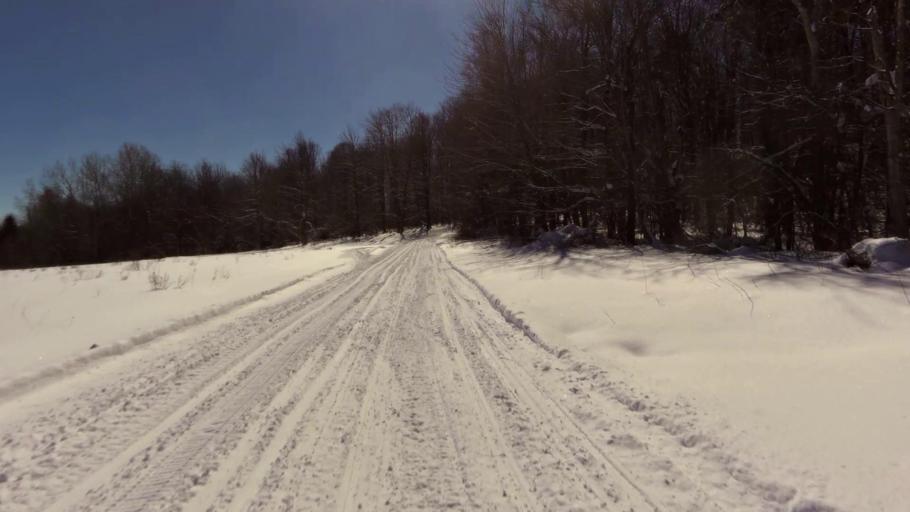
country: US
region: New York
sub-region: Chautauqua County
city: Mayville
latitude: 42.2152
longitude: -79.5347
